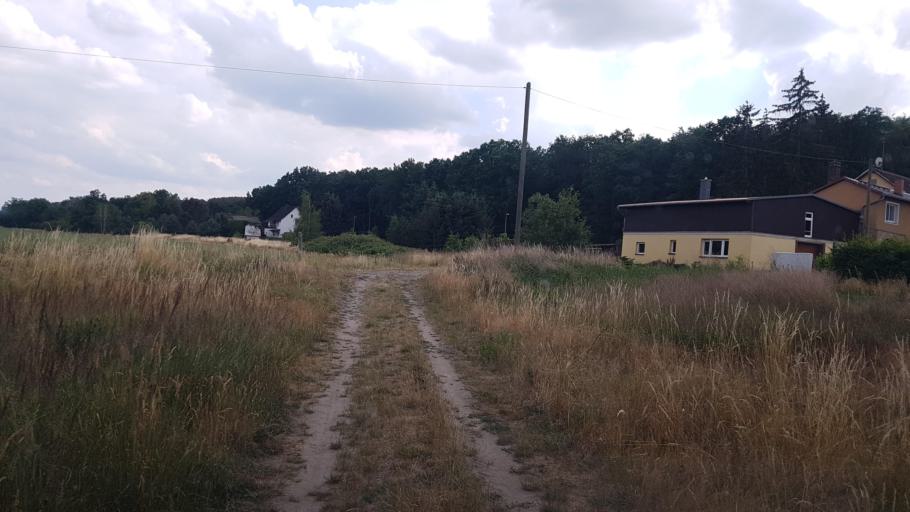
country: DE
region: Brandenburg
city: Golzow
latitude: 52.2352
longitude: 12.5851
